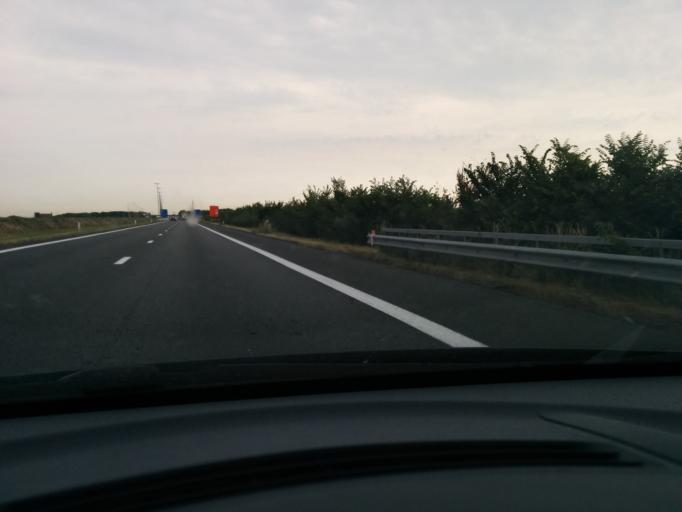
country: BE
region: Flanders
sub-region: Provincie West-Vlaanderen
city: Middelkerke
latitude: 51.1389
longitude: 2.8443
